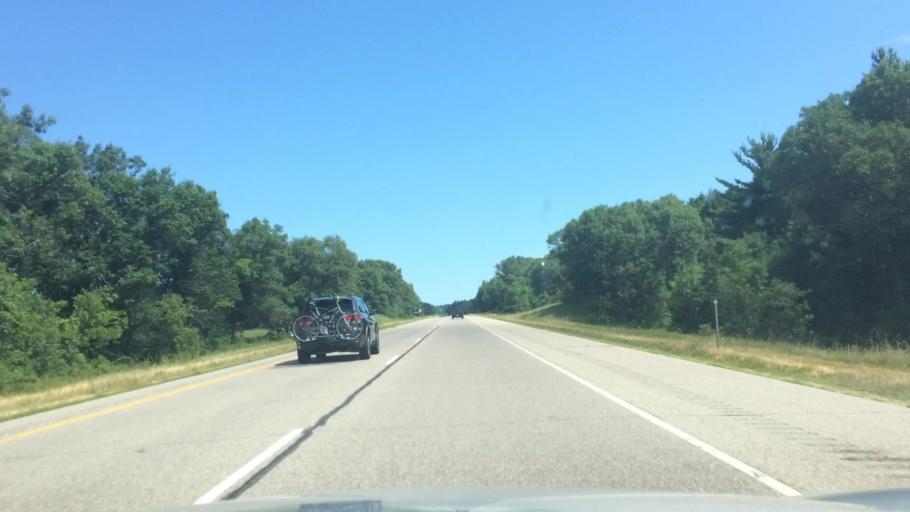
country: US
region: Wisconsin
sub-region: Marquette County
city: Westfield
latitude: 44.0695
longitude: -89.5386
